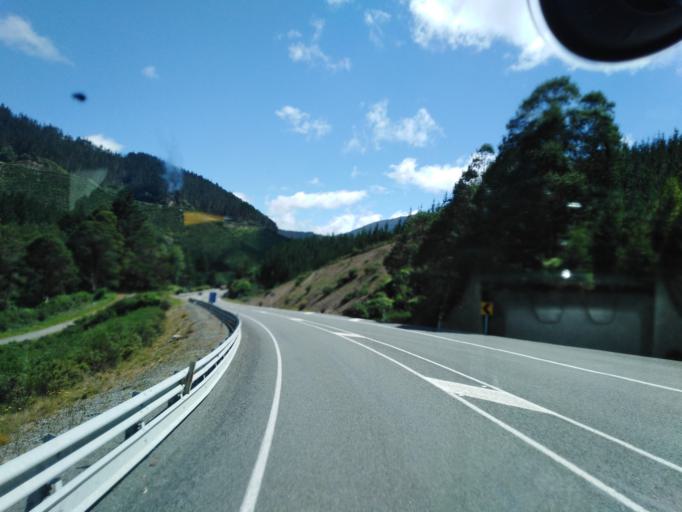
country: NZ
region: Nelson
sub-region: Nelson City
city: Nelson
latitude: -41.1843
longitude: 173.5600
